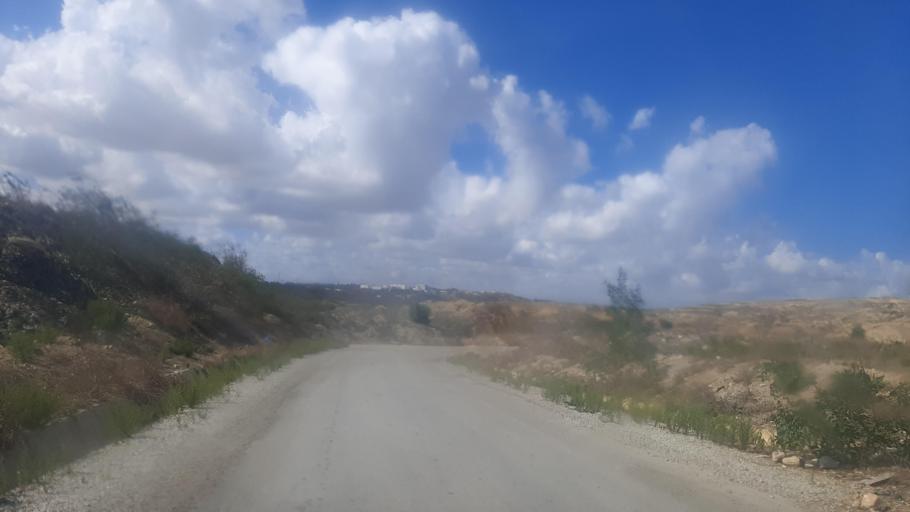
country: TN
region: Nabul
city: Nabeul
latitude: 36.4930
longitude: 10.7052
